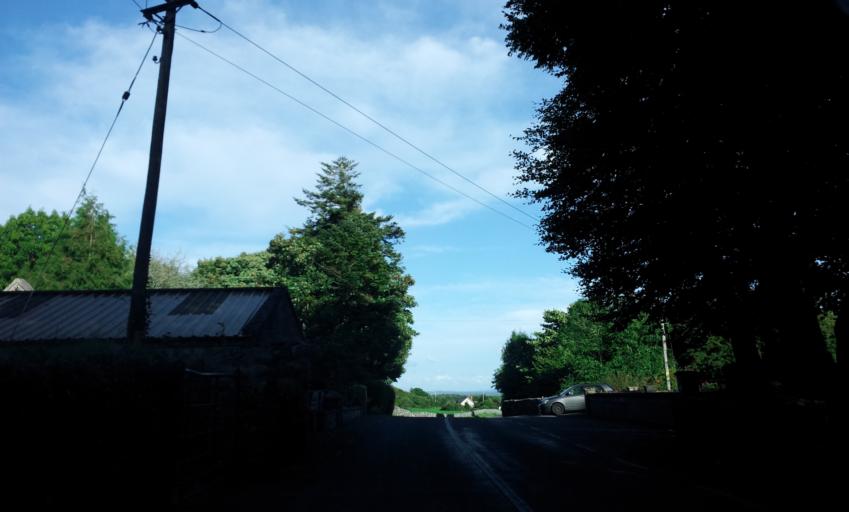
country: IE
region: Munster
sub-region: An Clar
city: Ennis
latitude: 52.9735
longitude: -9.0952
